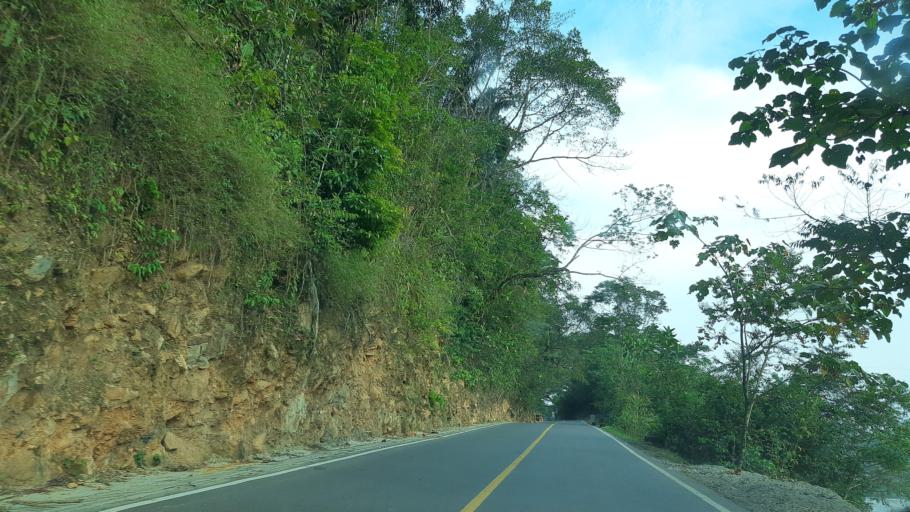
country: CO
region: Boyaca
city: San Luis de Gaceno
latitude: 4.8295
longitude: -73.2055
